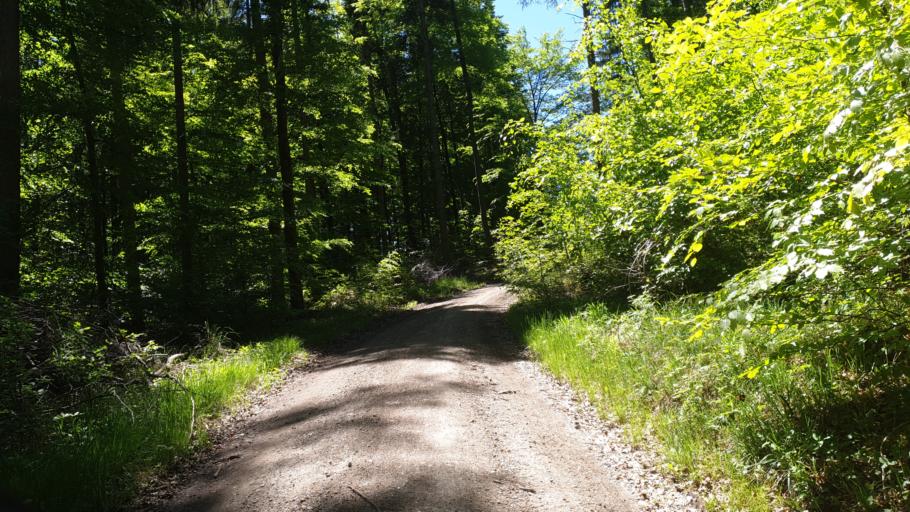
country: DE
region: Bavaria
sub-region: Upper Bavaria
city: Habach
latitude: 47.7762
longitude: 11.2579
